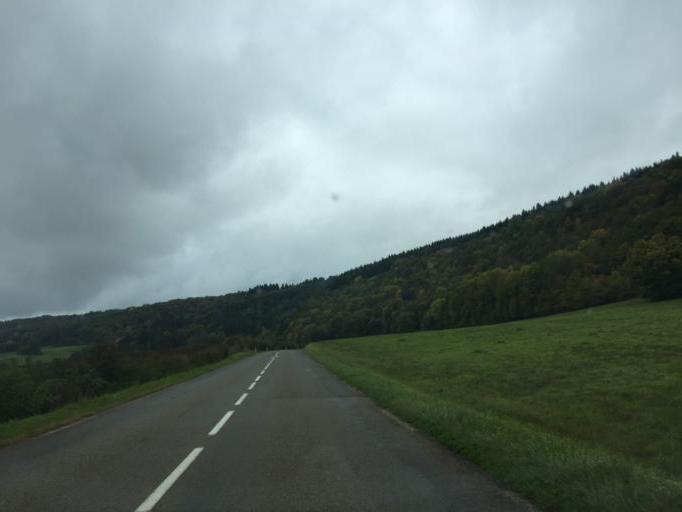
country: FR
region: Franche-Comte
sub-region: Departement du Jura
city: Orgelet
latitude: 46.5045
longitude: 5.5949
